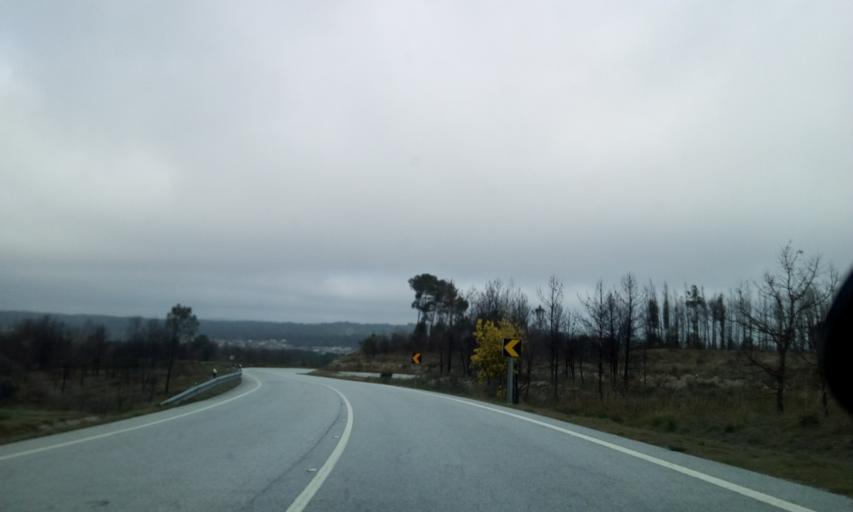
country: PT
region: Guarda
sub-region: Fornos de Algodres
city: Fornos de Algodres
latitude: 40.7072
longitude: -7.4834
